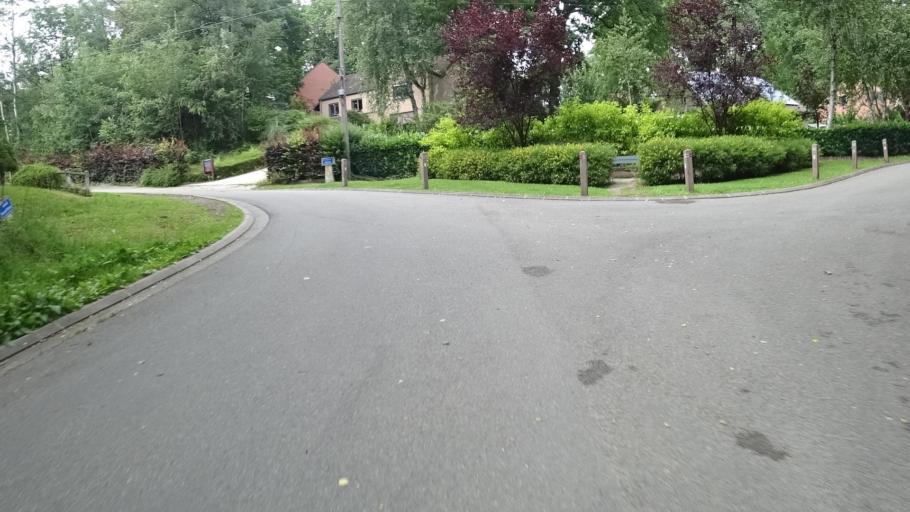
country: BE
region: Wallonia
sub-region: Province du Brabant Wallon
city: Villers-la-Ville
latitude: 50.5759
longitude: 4.5421
